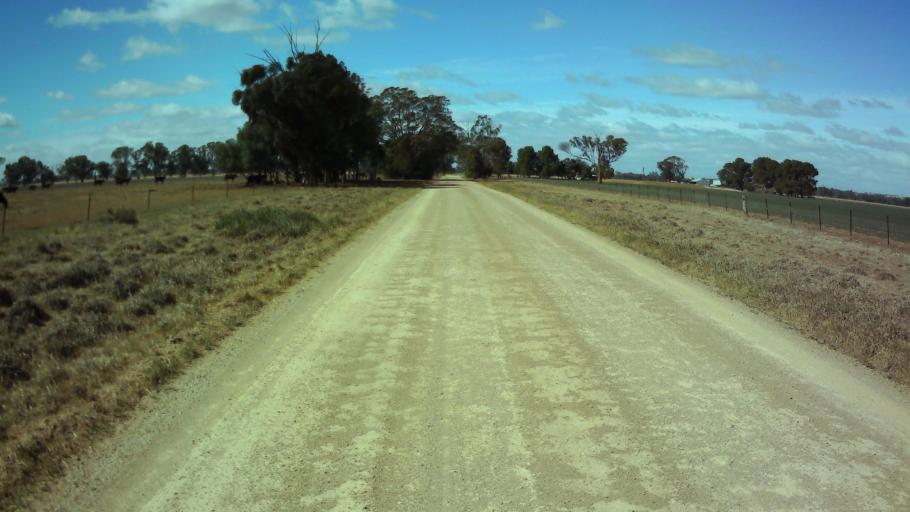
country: AU
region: New South Wales
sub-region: Weddin
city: Grenfell
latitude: -34.0260
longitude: 148.3181
